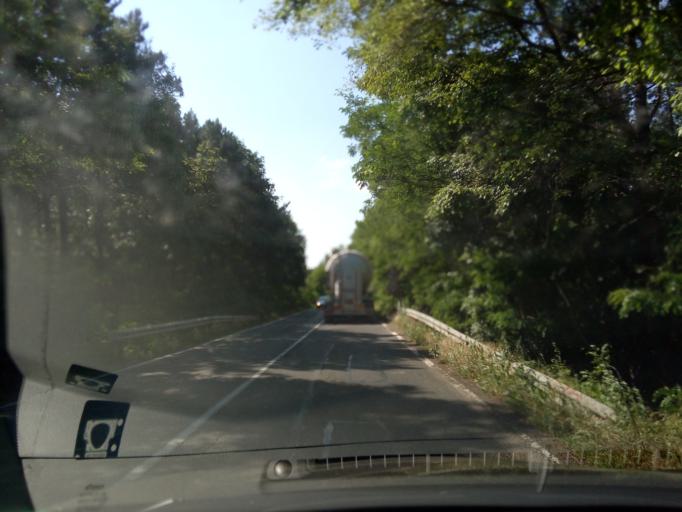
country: BG
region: Burgas
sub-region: Obshtina Nesebur
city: Sveti Vlas
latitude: 42.7667
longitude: 27.7861
